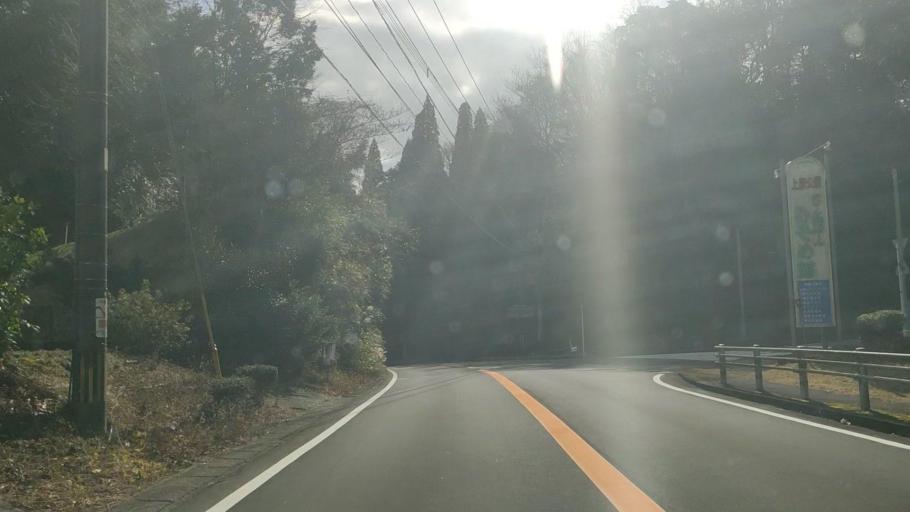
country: JP
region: Kagoshima
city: Kajiki
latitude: 31.8277
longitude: 130.6888
